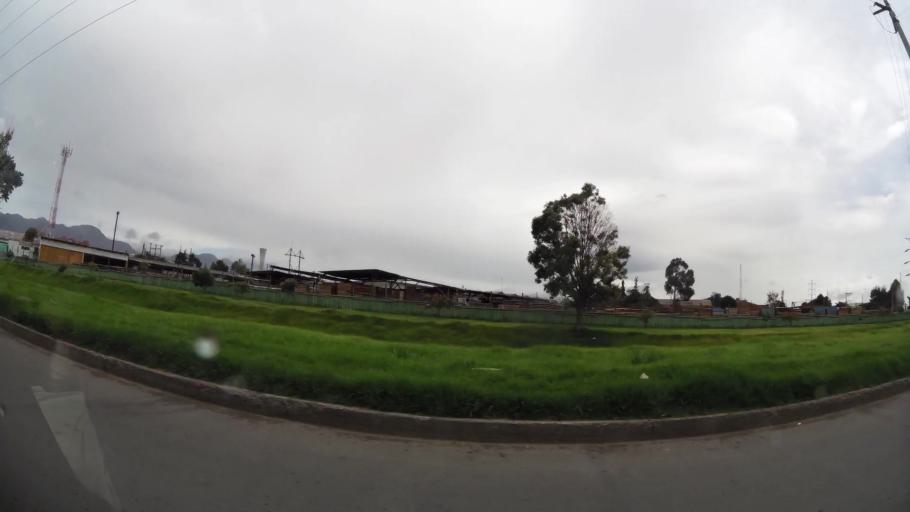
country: CO
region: Bogota D.C.
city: Bogota
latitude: 4.6496
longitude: -74.1132
